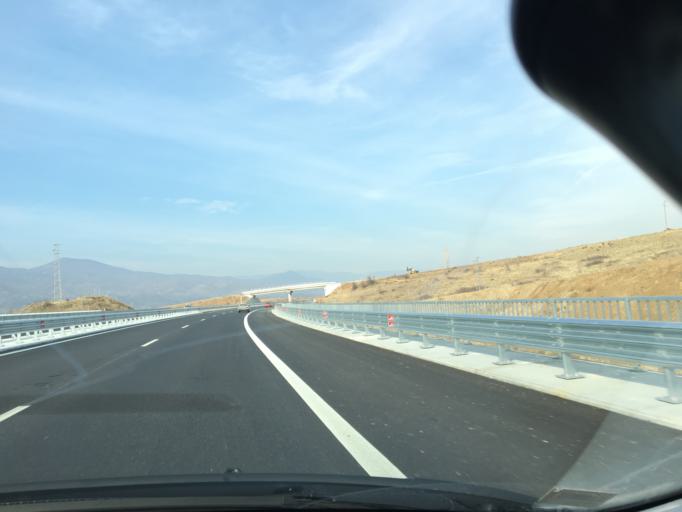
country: BG
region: Blagoevgrad
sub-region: Obshtina Sandanski
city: Sandanski
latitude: 41.5290
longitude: 23.2630
